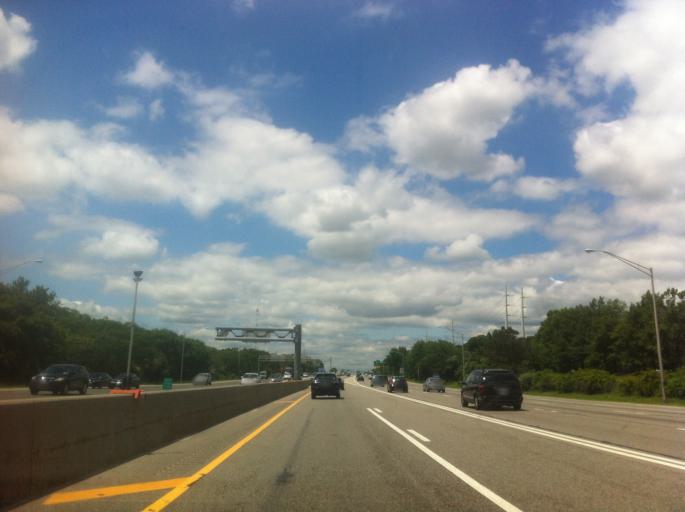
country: US
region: New York
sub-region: Suffolk County
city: Islandia
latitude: 40.8089
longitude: -73.1649
